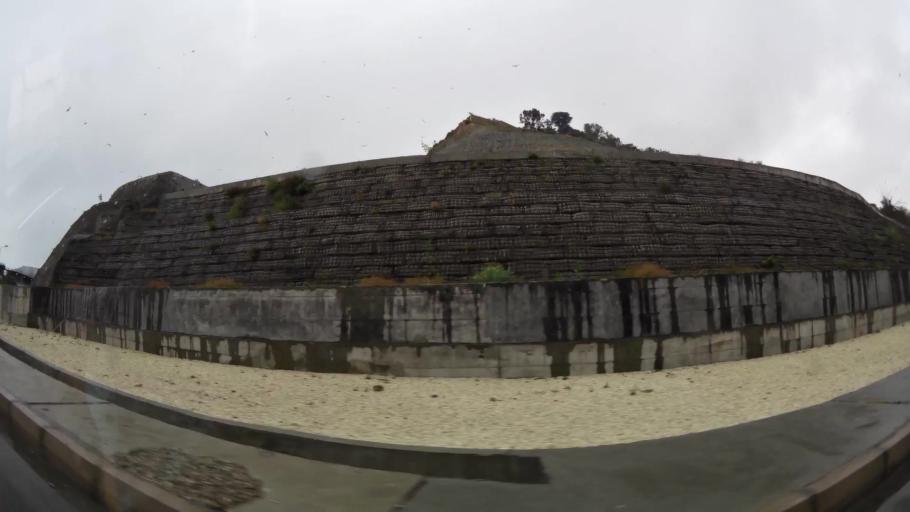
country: MA
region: Taza-Al Hoceima-Taounate
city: Al Hoceima
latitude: 35.2483
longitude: -3.9249
